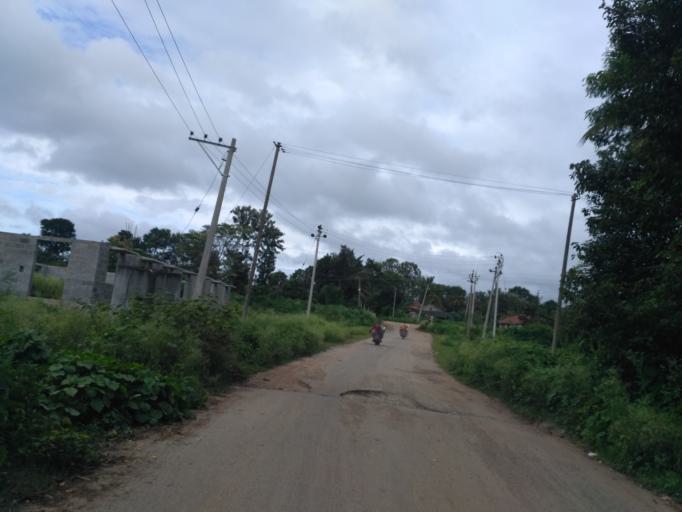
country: IN
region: Karnataka
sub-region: Hassan
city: Gorur
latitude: 12.8242
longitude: 76.0913
